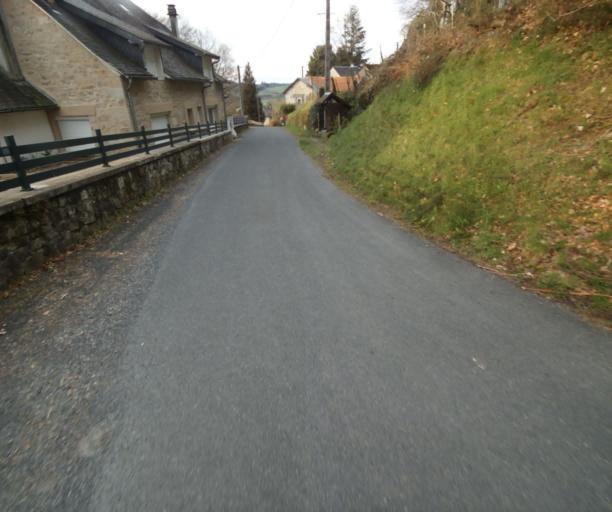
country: FR
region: Limousin
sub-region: Departement de la Correze
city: Correze
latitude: 45.3730
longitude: 1.8710
